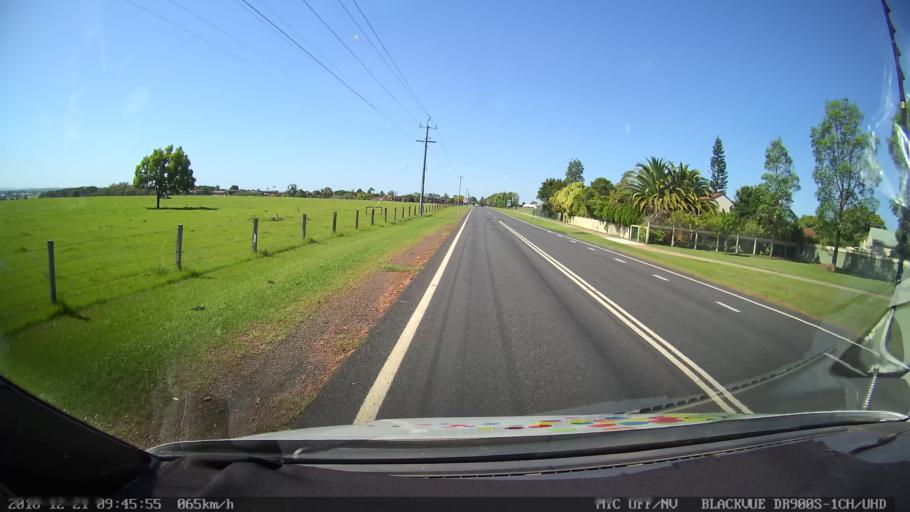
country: AU
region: New South Wales
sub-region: Clarence Valley
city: Grafton
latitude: -29.6342
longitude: 152.9275
